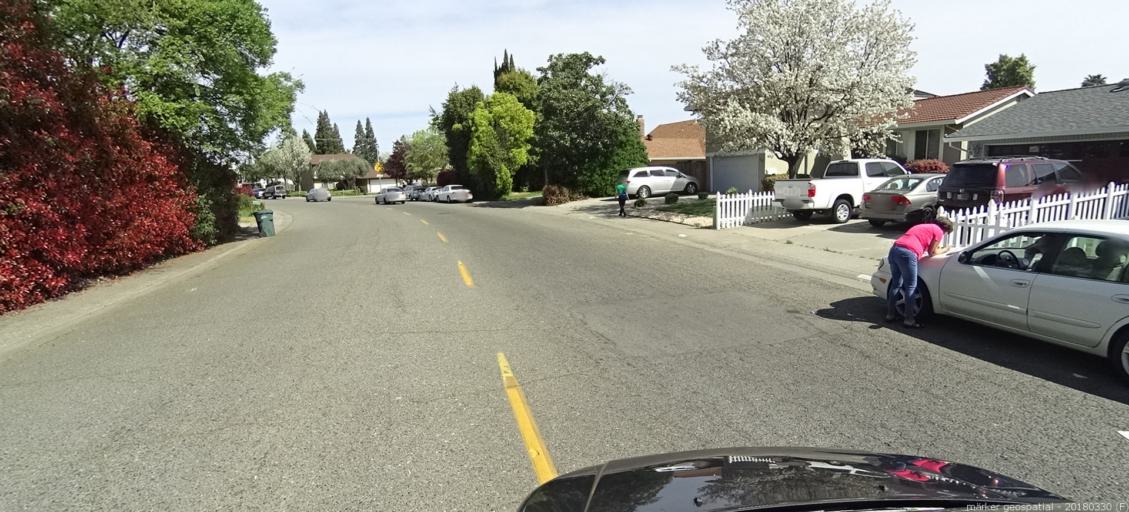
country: US
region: California
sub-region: Sacramento County
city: Rosemont
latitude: 38.5579
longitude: -121.3621
